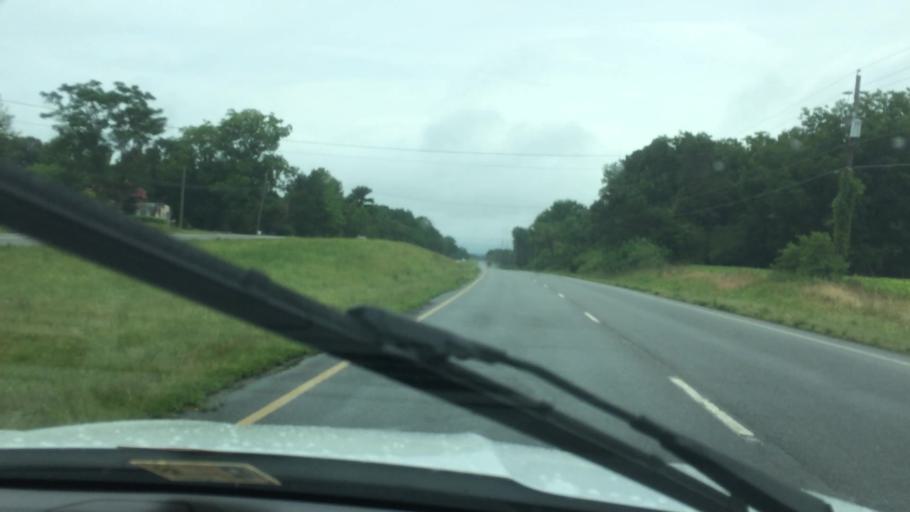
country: US
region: Virginia
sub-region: King William County
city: West Point
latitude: 37.5476
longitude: -76.7381
